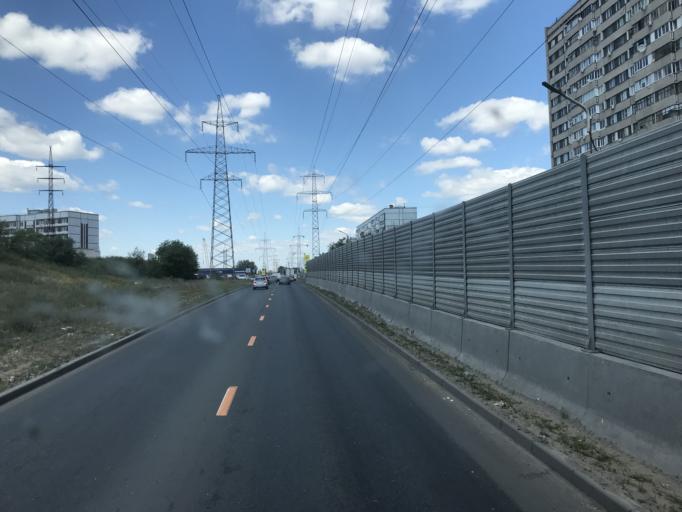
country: RU
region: Samara
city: Zhigulevsk
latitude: 53.4737
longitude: 49.5121
